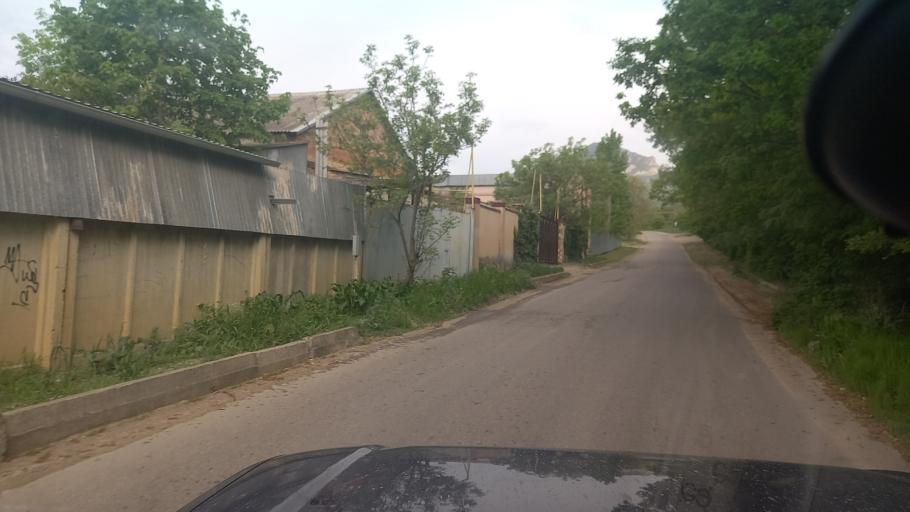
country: RU
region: Stavropol'skiy
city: Pyatigorsk
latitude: 44.0671
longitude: 43.0550
